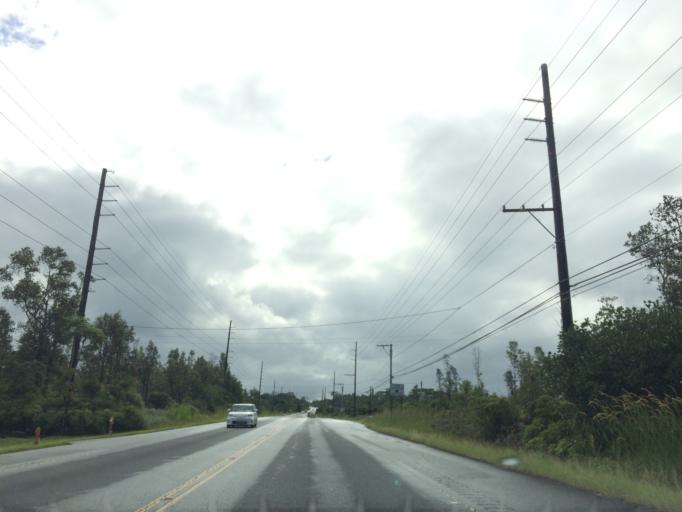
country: US
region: Hawaii
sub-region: Hawaii County
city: Orchidlands Estates
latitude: 19.5551
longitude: -154.9876
